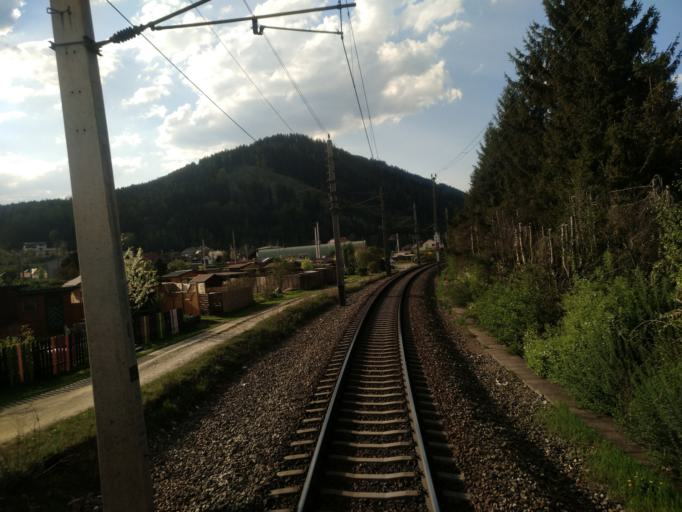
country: AT
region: Styria
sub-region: Politischer Bezirk Leoben
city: Sankt Michael in Obersteiermark
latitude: 47.3411
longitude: 15.0125
